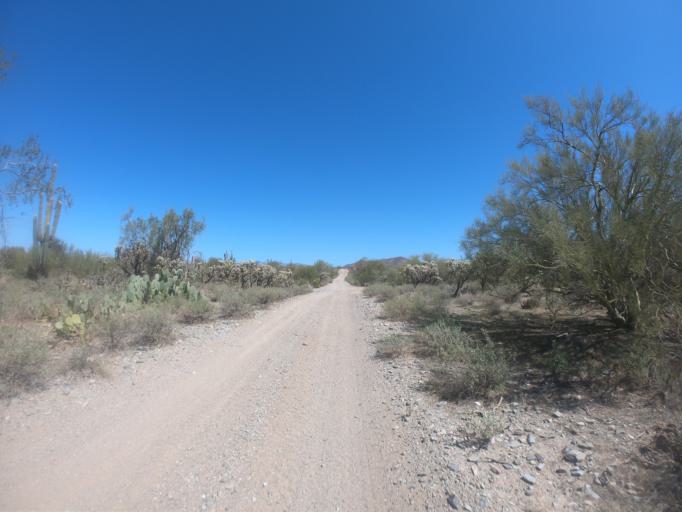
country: US
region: Arizona
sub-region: Pinal County
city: Gold Camp
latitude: 33.2583
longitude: -111.2712
